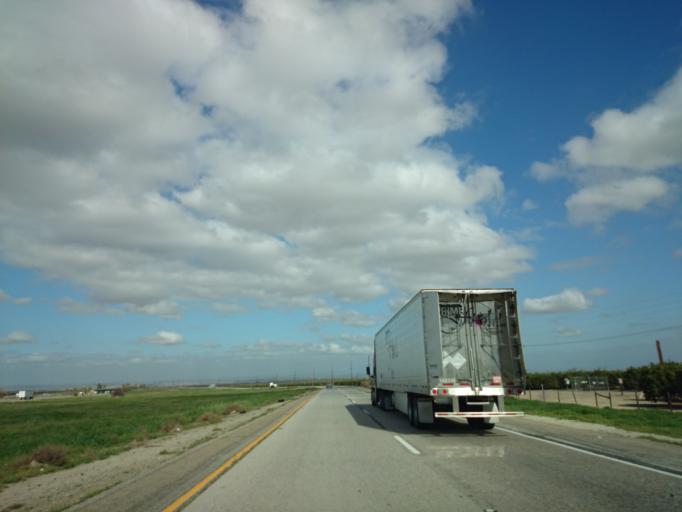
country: US
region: California
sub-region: Kern County
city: Frazier Park
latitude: 35.0103
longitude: -118.9520
